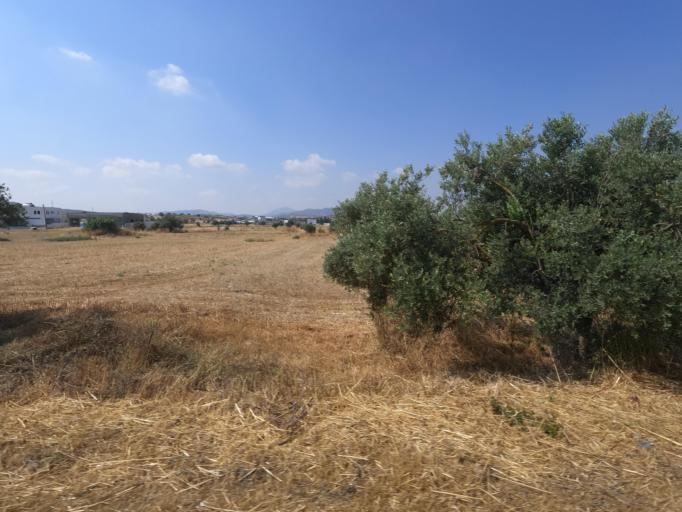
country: CY
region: Lefkosia
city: Lympia
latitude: 35.0013
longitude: 33.4474
